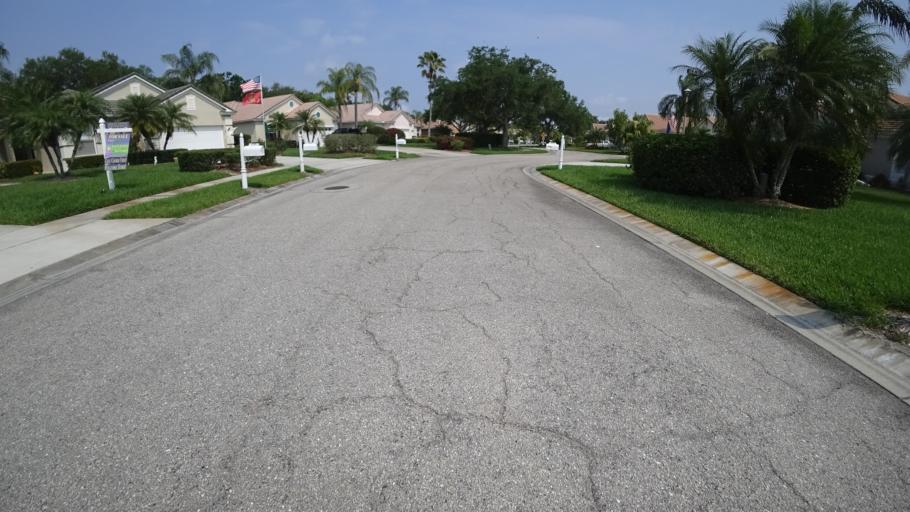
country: US
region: Florida
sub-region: Manatee County
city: Samoset
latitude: 27.4562
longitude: -82.5123
